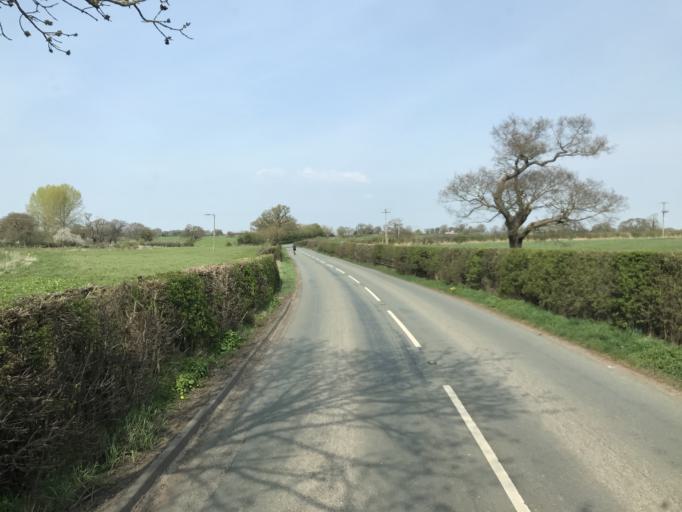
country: GB
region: England
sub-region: Cheshire West and Chester
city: Eccleston
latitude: 53.1510
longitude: -2.8617
